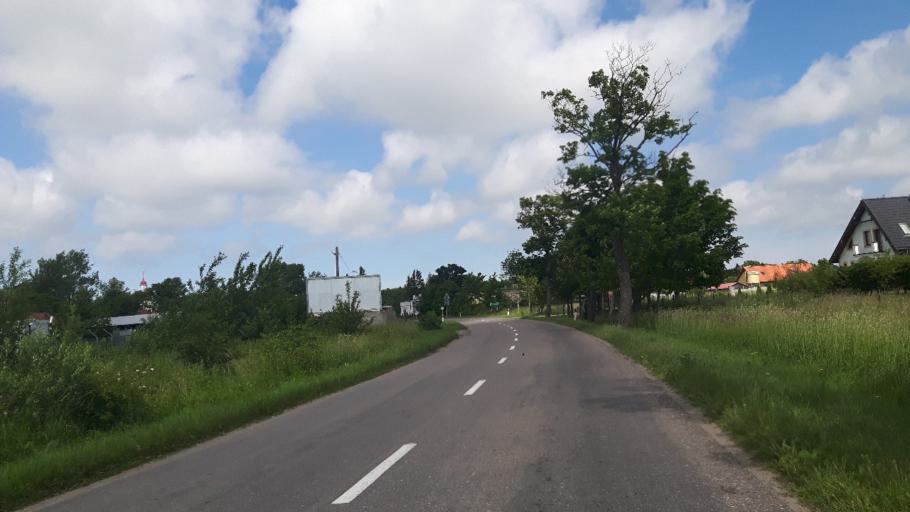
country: PL
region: Pomeranian Voivodeship
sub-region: Powiat slupski
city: Ustka
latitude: 54.5352
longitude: 16.8209
